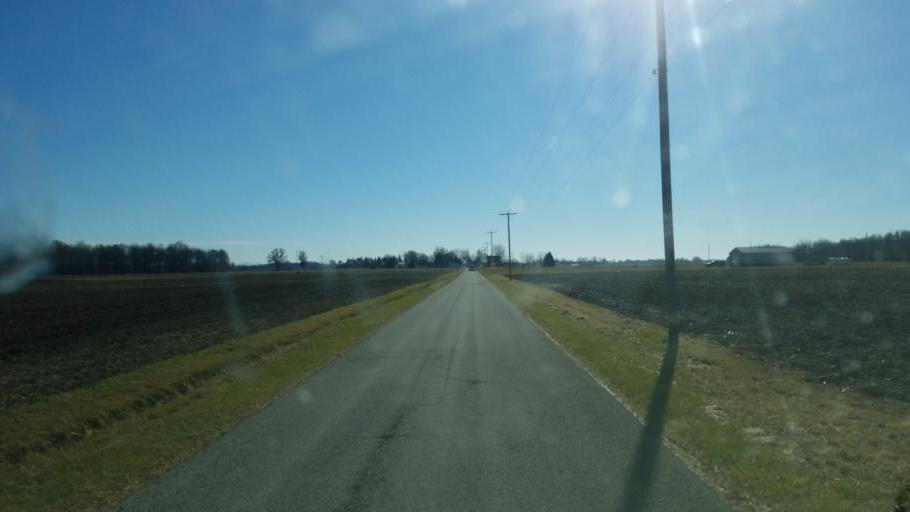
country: US
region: Ohio
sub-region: Crawford County
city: Galion
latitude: 40.7734
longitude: -82.8387
